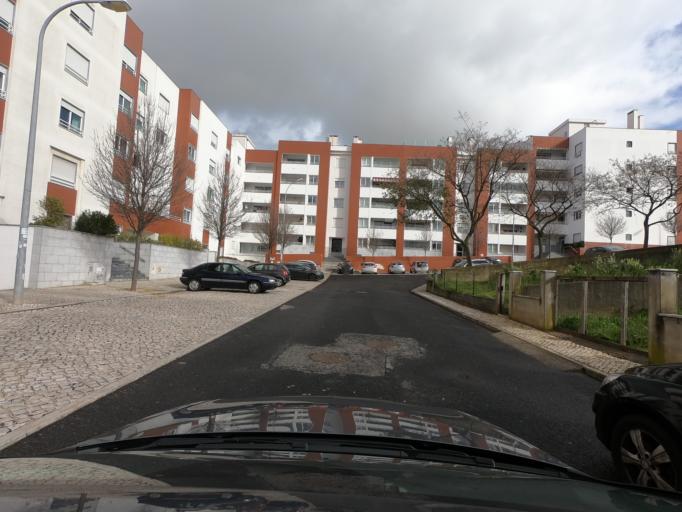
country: PT
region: Lisbon
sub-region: Cascais
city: Sao Domingos de Rana
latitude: 38.7102
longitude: -9.3262
